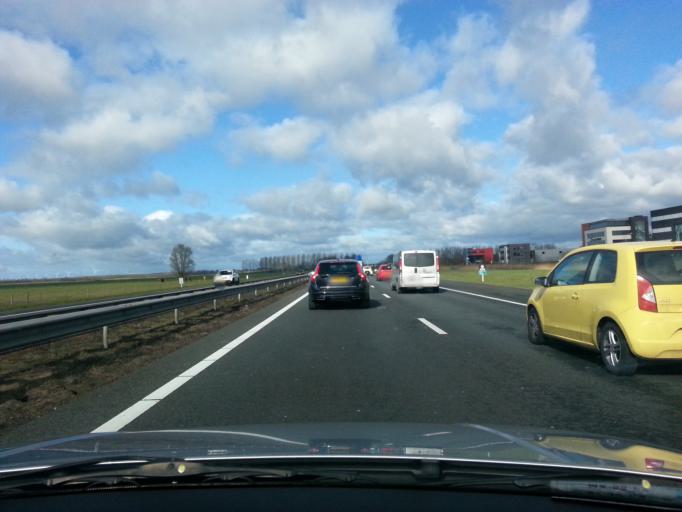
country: NL
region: Gelderland
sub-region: Gemeente Nijkerk
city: Nijkerk
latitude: 52.2292
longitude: 5.4578
